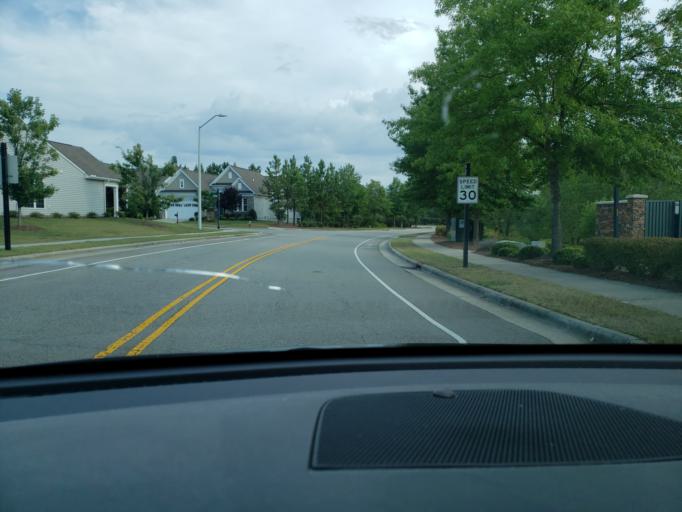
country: US
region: North Carolina
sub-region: Wake County
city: Green Level
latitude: 35.8311
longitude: -78.9136
